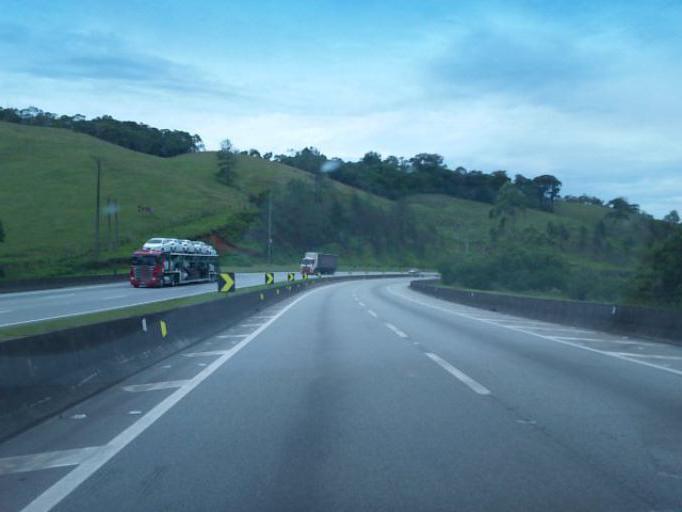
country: BR
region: Sao Paulo
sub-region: Juquitiba
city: Juquitiba
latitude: -24.0011
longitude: -47.1513
